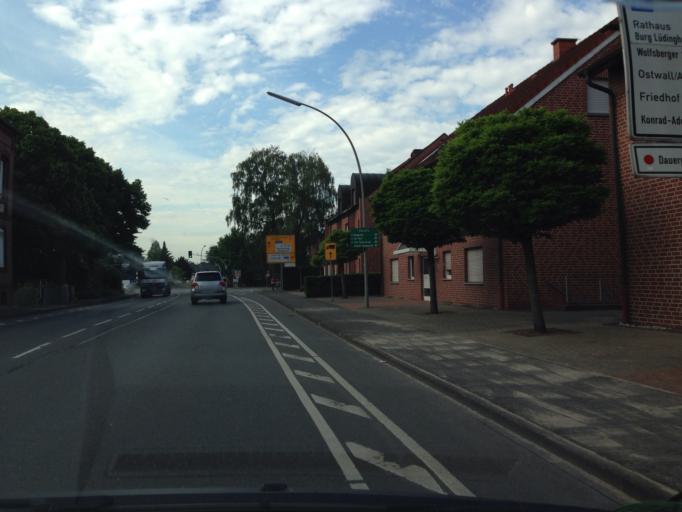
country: DE
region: North Rhine-Westphalia
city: Ludinghausen
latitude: 51.7765
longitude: 7.4479
